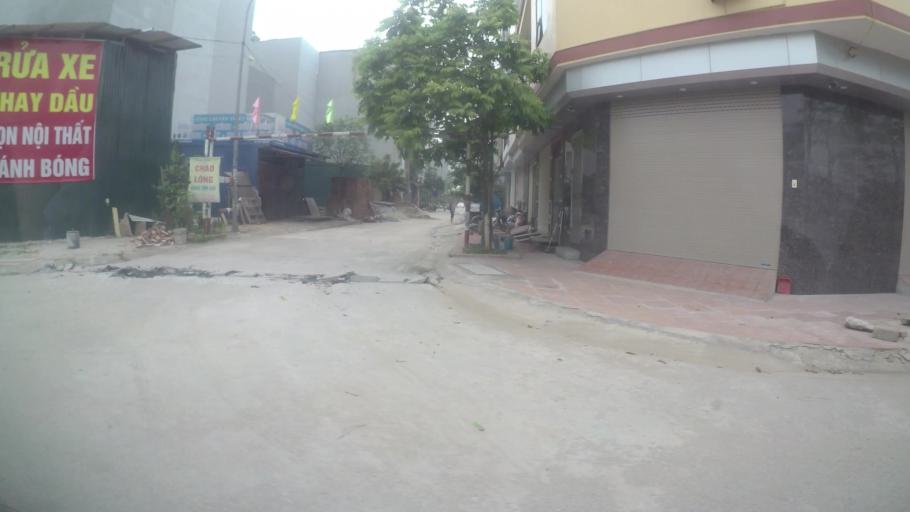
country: VN
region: Ha Noi
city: Ha Dong
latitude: 20.9728
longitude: 105.7489
